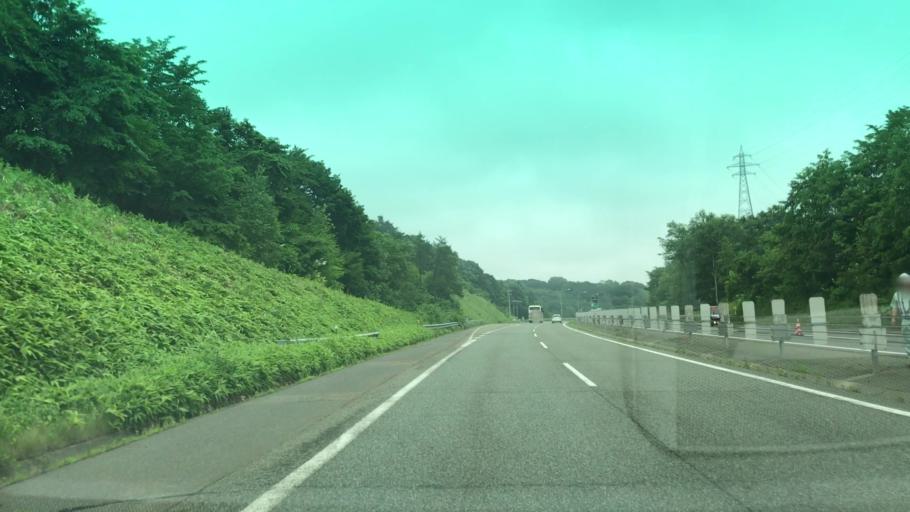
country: JP
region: Hokkaido
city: Tomakomai
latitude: 42.6640
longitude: 141.5882
